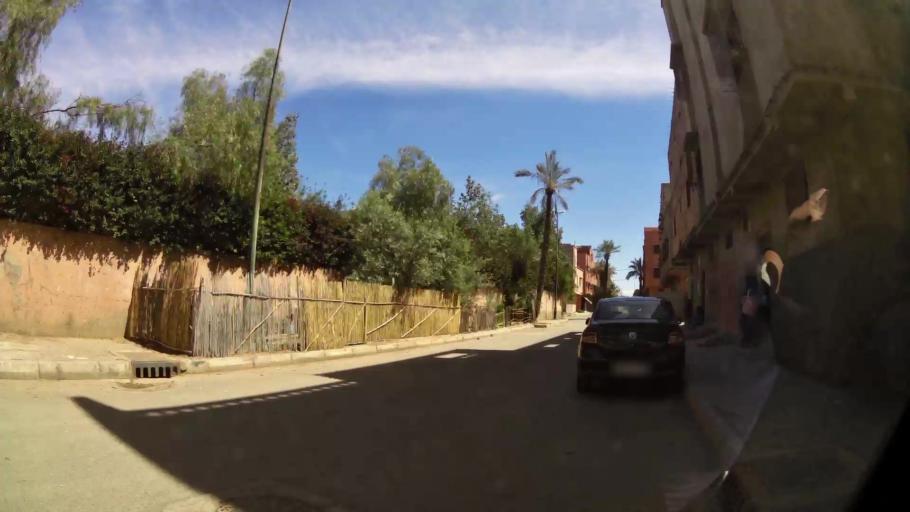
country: MA
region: Marrakech-Tensift-Al Haouz
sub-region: Marrakech
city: Marrakesh
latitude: 31.6649
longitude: -7.9840
